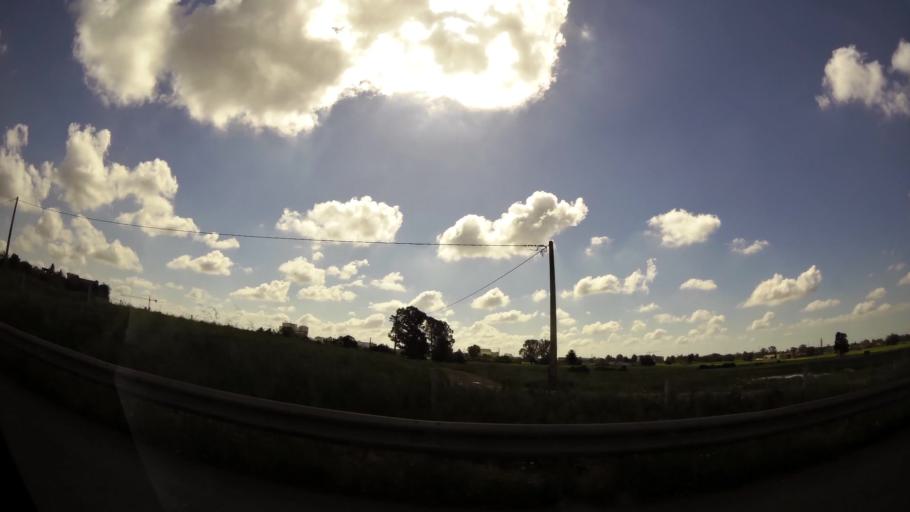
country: MA
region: Grand Casablanca
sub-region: Nouaceur
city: Bouskoura
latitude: 33.4442
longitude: -7.6317
